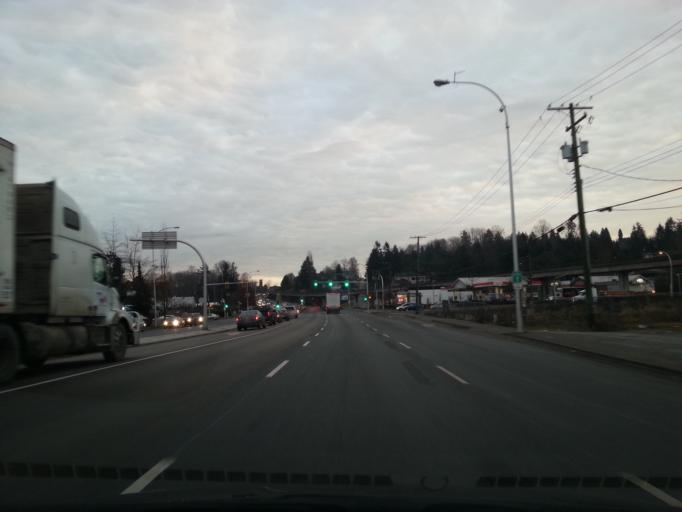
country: CA
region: British Columbia
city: New Westminster
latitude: 49.2062
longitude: -122.8690
